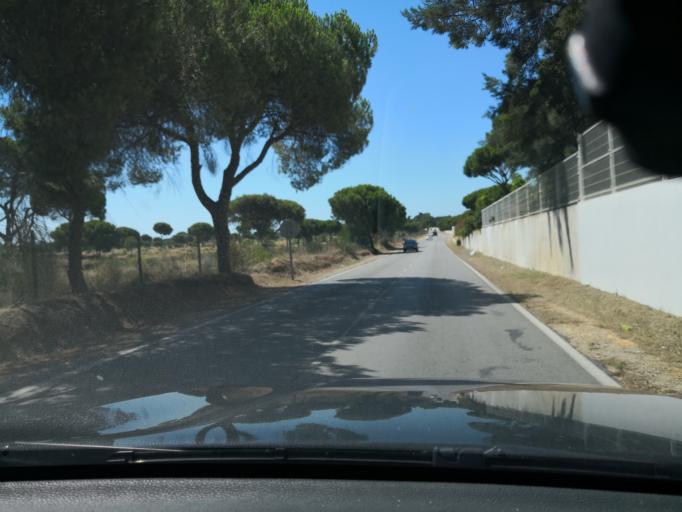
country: PT
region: Faro
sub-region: Loule
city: Vilamoura
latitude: 37.0887
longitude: -8.1015
